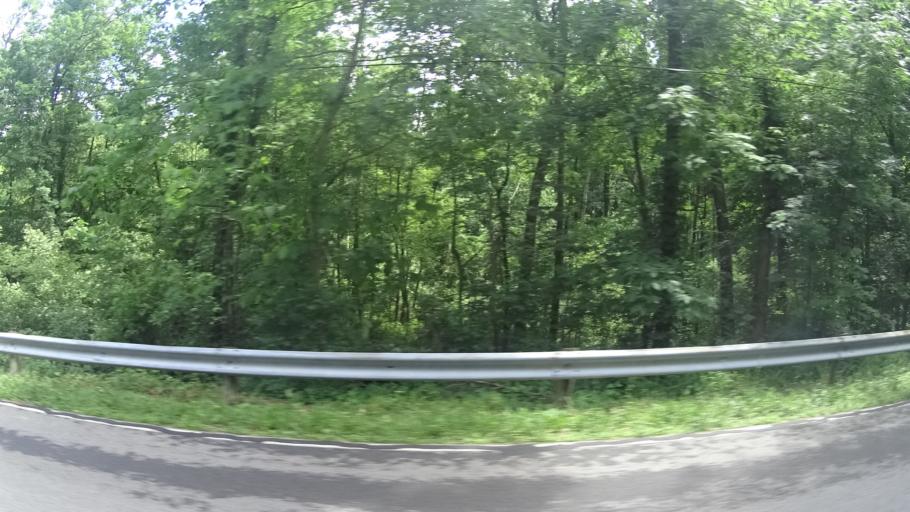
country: US
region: Ohio
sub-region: Erie County
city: Milan
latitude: 41.3192
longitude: -82.5601
